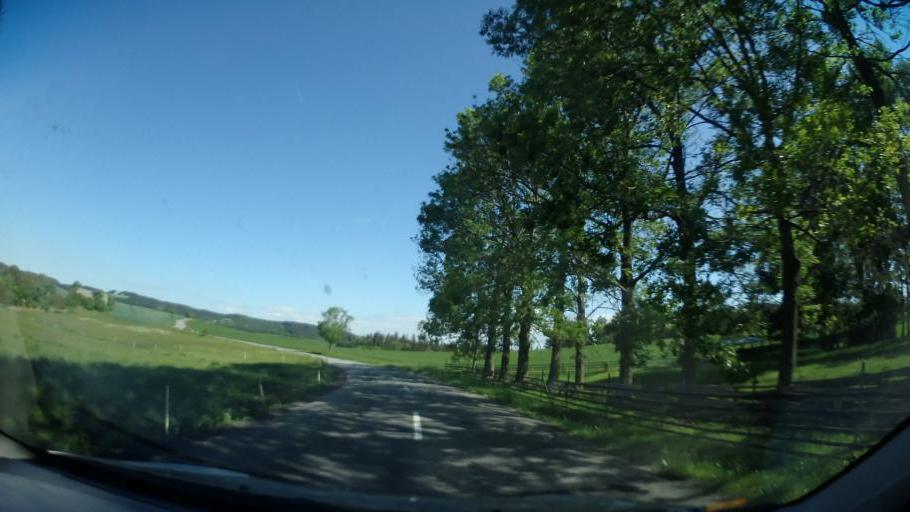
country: CZ
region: South Moravian
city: Velke Opatovice
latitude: 49.6157
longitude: 16.6093
